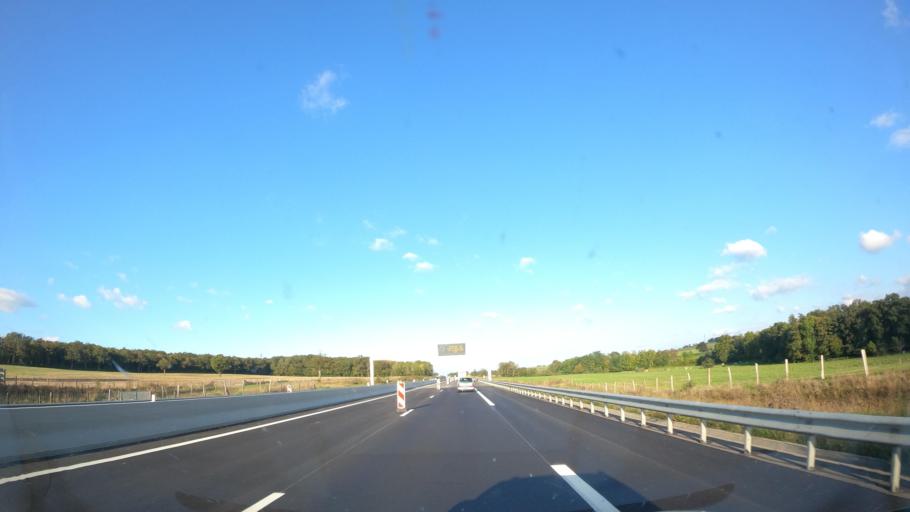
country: FR
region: Bourgogne
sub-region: Departement de Saone-et-Loire
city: Blanzy
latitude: 46.7077
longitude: 4.4227
